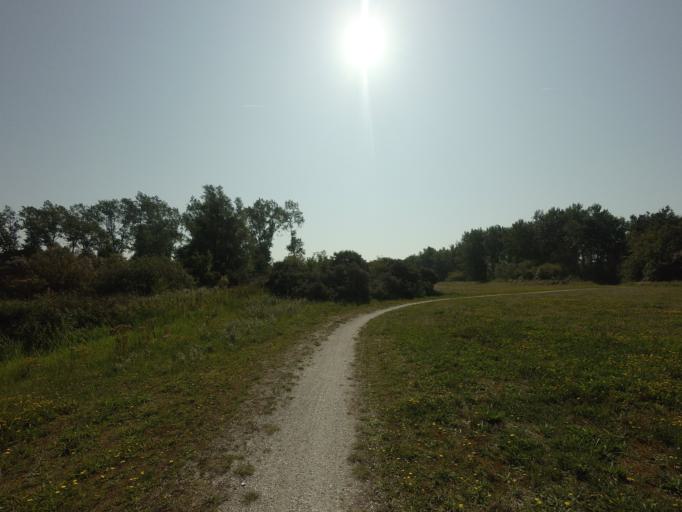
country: NL
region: Groningen
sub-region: Gemeente De Marne
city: Ulrum
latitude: 53.3948
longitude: 6.2540
